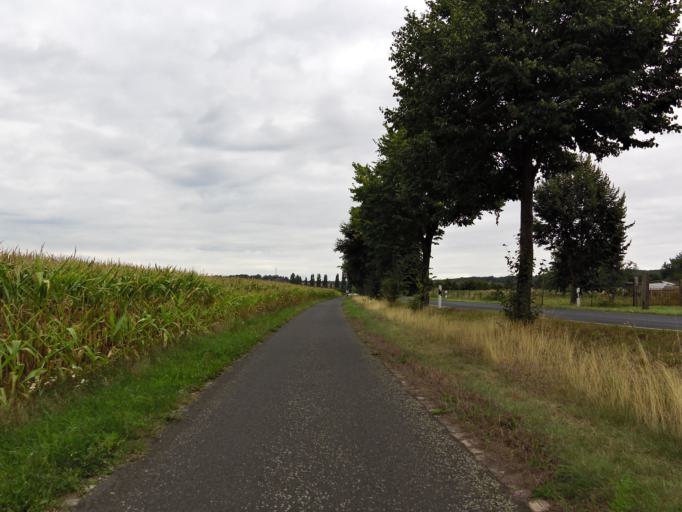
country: DE
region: Saxony
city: Weissig
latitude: 51.2161
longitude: 13.4094
